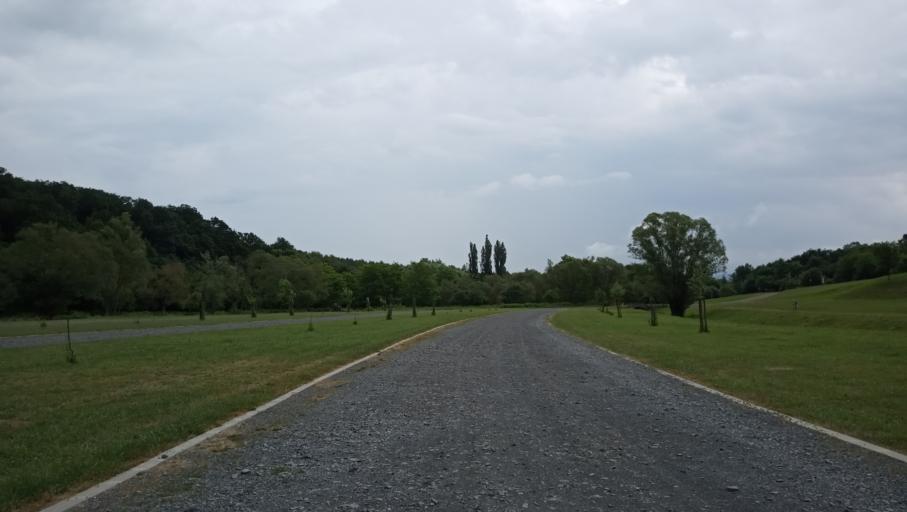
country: HU
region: Nograd
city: Matraverebely
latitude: 48.0006
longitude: 19.7652
